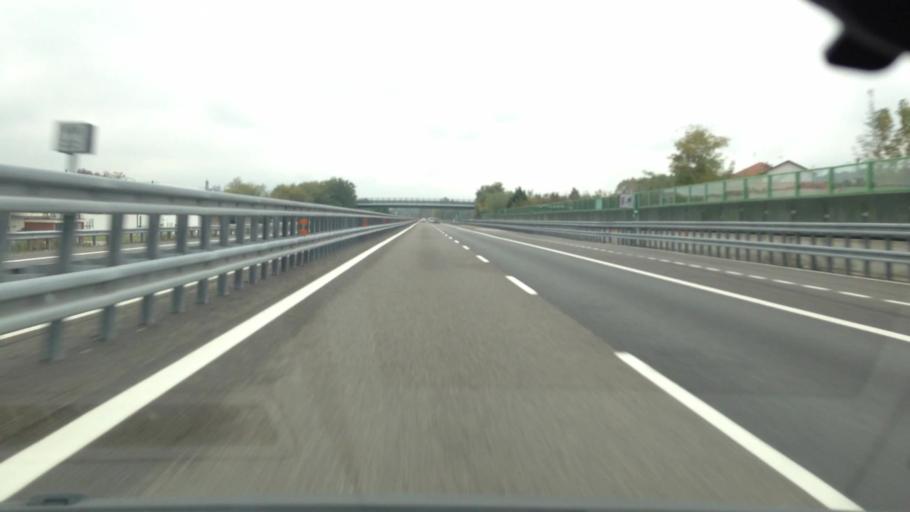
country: IT
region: Piedmont
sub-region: Provincia di Asti
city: Cantarana
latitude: 44.9064
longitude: 8.0539
